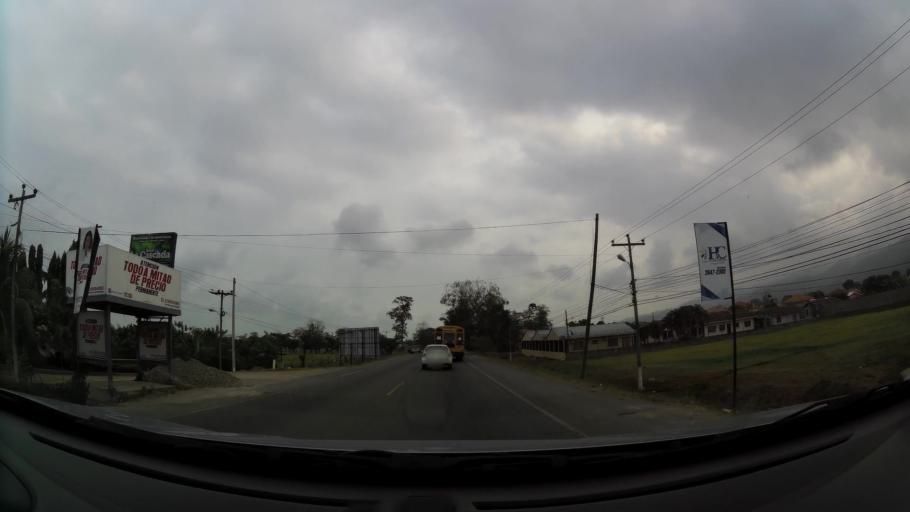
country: HN
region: Yoro
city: El Progreso
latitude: 15.4347
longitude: -87.7946
